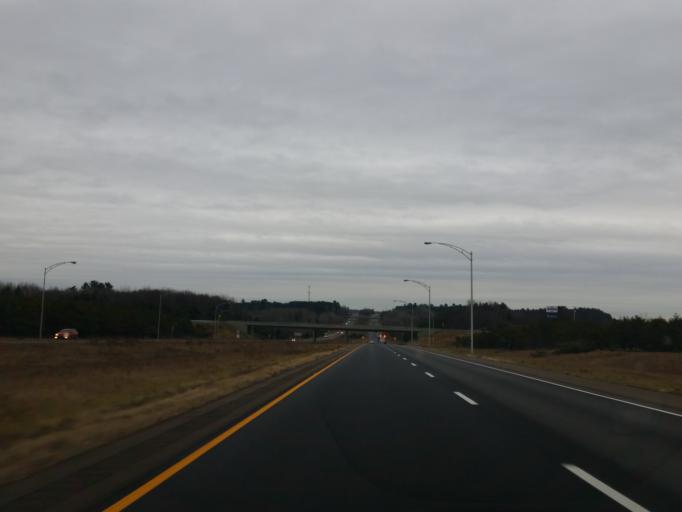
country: CA
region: Quebec
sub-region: Capitale-Nationale
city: Cap-Sante
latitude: 46.6977
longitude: -71.8953
